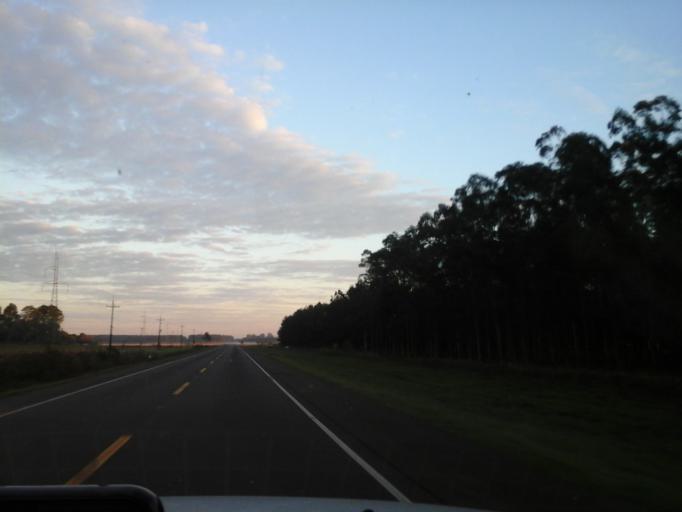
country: PY
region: Itapua
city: General Delgado
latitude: -27.0710
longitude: -56.6069
